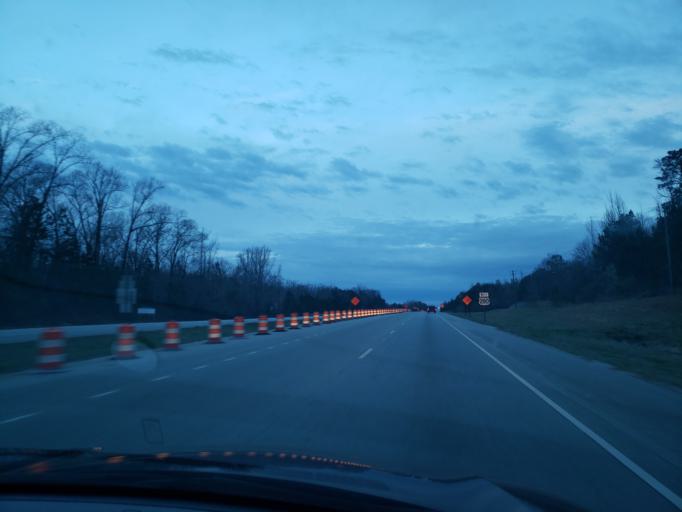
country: US
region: Alabama
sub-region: Lee County
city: Auburn
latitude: 32.6655
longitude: -85.4734
